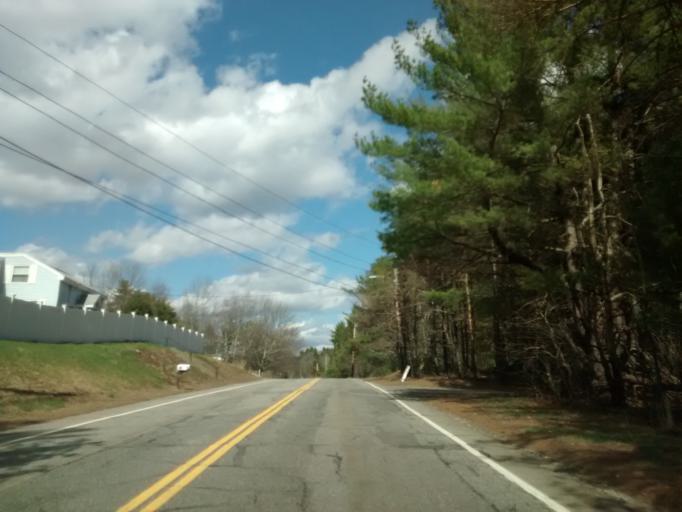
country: US
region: Massachusetts
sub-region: Worcester County
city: Upton
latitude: 42.1841
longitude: -71.6000
